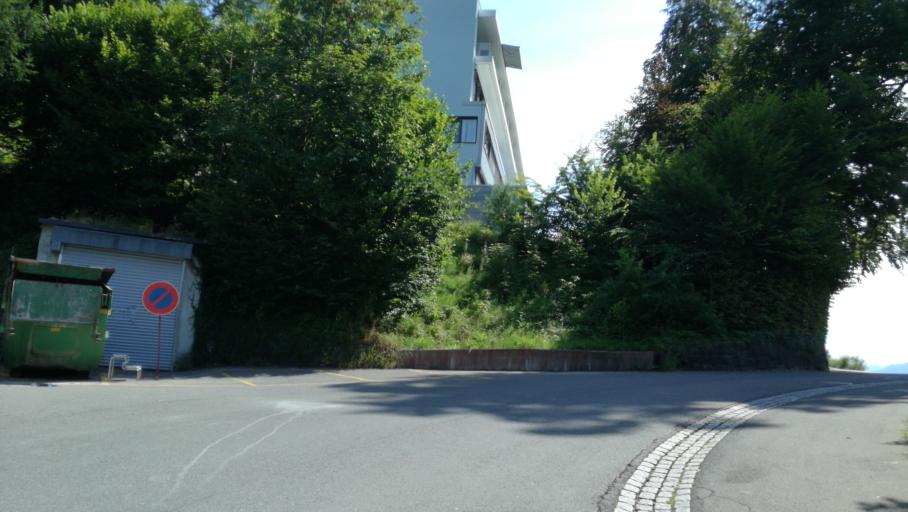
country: CH
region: Zug
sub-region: Zug
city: Unterageri
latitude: 47.1411
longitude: 8.5900
